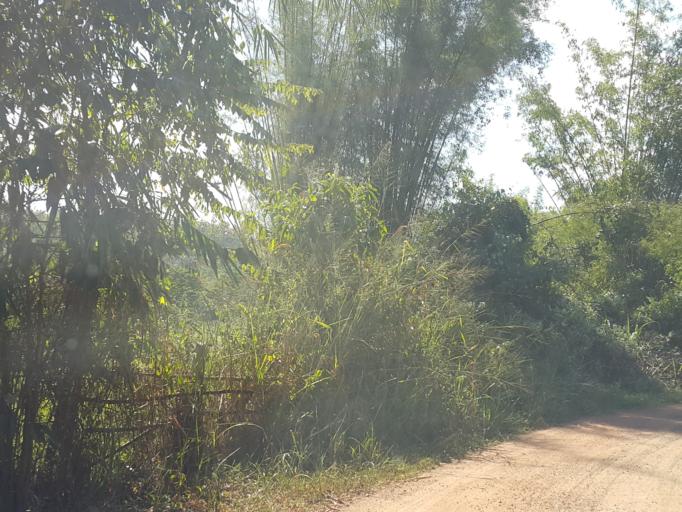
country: TH
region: Chiang Mai
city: Mae Taeng
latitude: 18.9588
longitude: 98.9109
